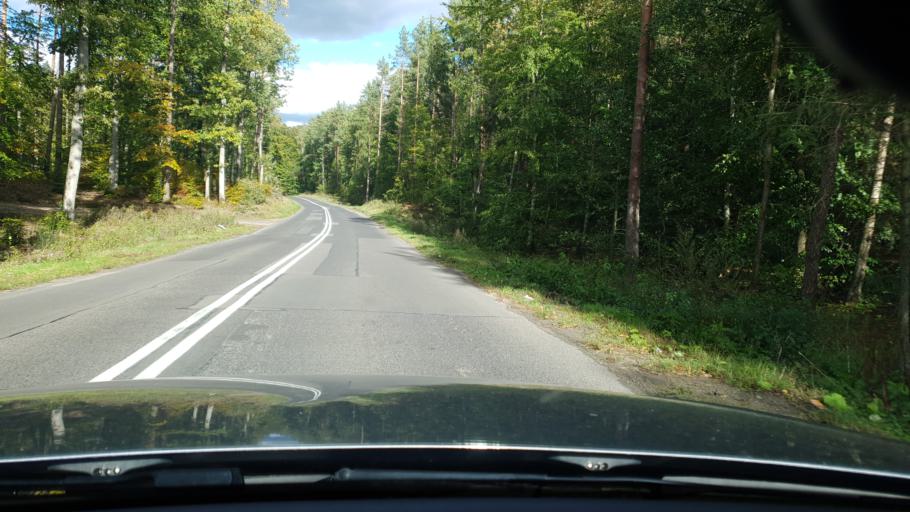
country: PL
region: Pomeranian Voivodeship
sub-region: Powiat wejherowski
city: Koleczkowo
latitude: 54.5035
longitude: 18.3671
